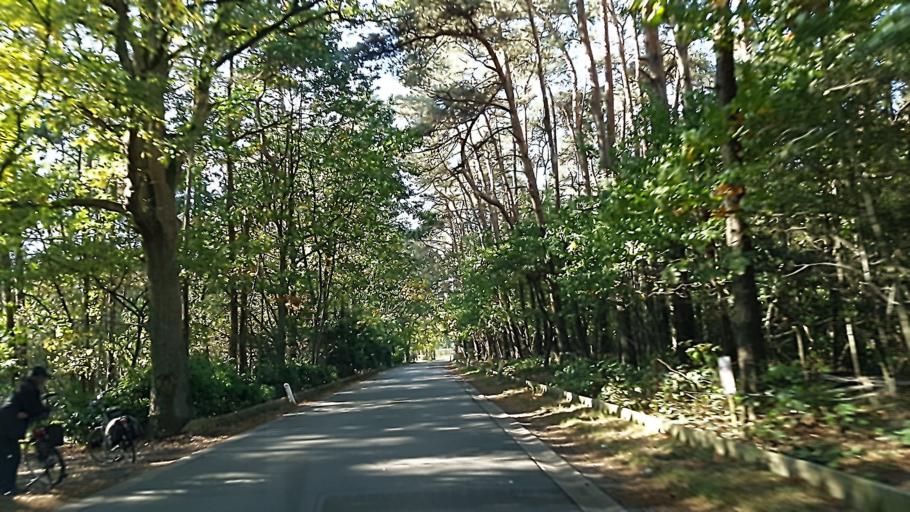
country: BE
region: Flanders
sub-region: Provincie Antwerpen
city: Essen
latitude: 51.4268
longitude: 4.4336
